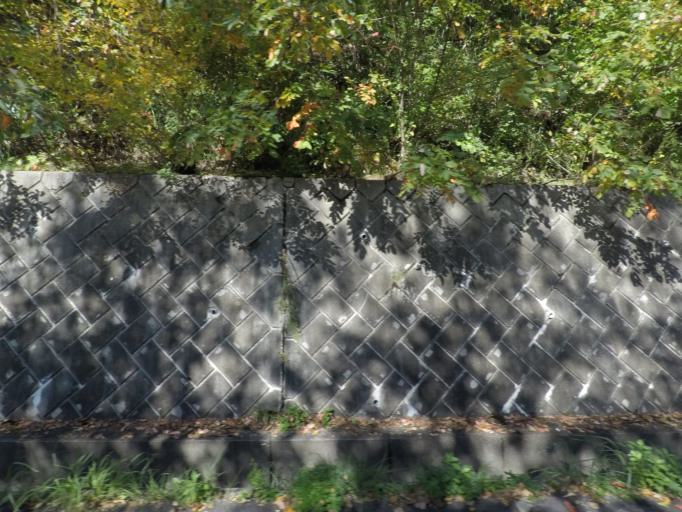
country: JP
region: Nagano
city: Shiojiri
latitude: 35.9877
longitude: 137.7687
